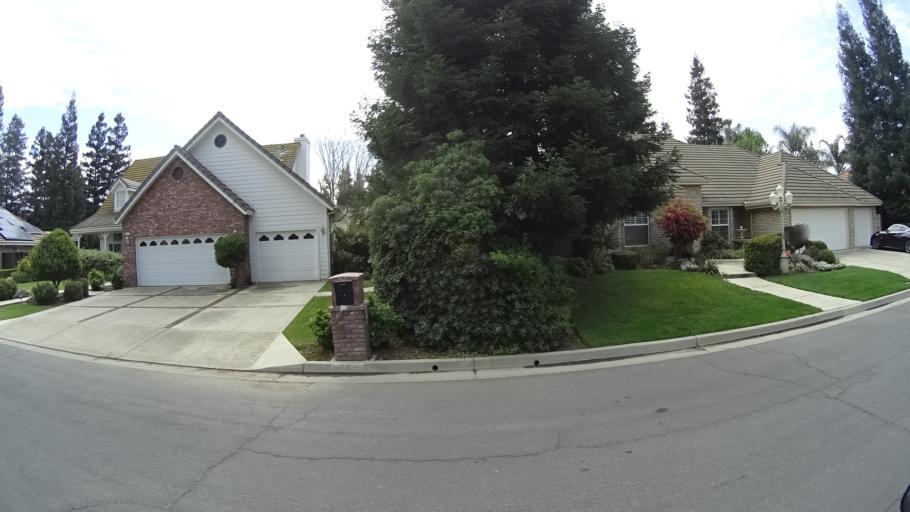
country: US
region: California
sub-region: Fresno County
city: West Park
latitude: 36.8407
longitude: -119.8823
